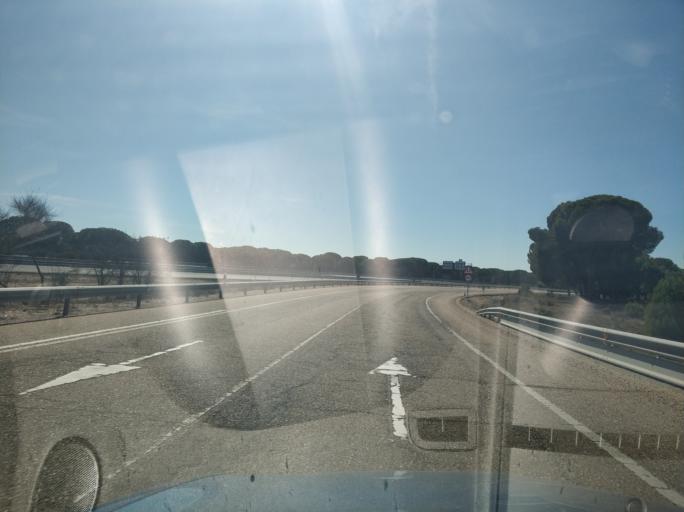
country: ES
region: Castille and Leon
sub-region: Provincia de Valladolid
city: Tordesillas
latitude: 41.4890
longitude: -5.0262
